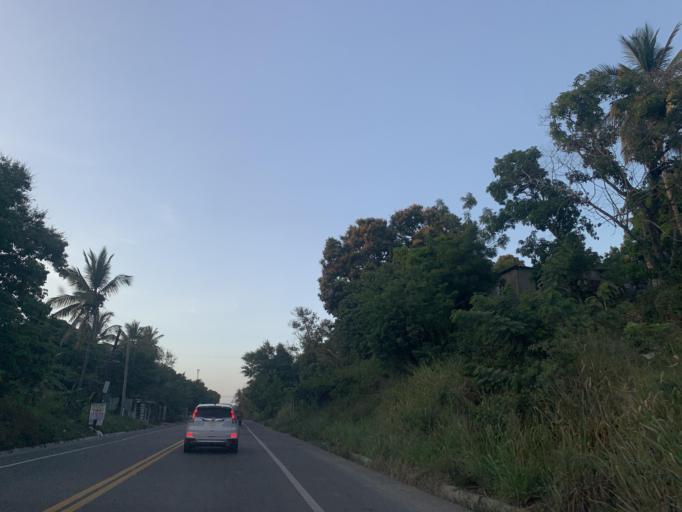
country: DO
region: Puerto Plata
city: Imbert
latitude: 19.7753
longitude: -70.8443
